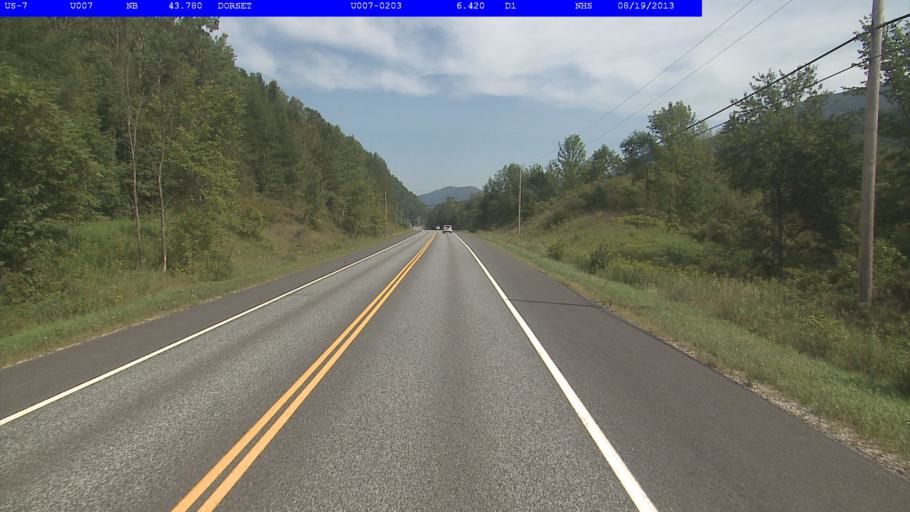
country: US
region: Vermont
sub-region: Bennington County
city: Manchester Center
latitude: 43.3007
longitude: -72.9959
